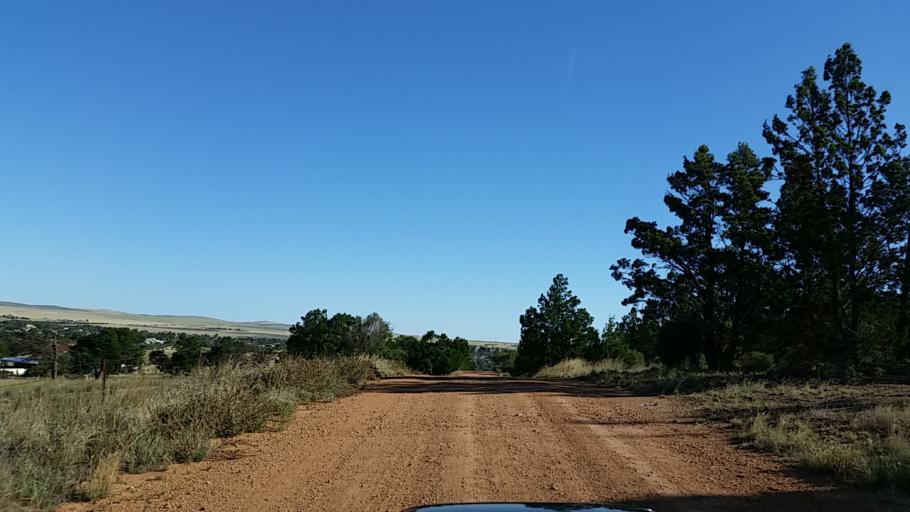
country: AU
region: South Australia
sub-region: Peterborough
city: Peterborough
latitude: -32.9599
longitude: 138.8317
